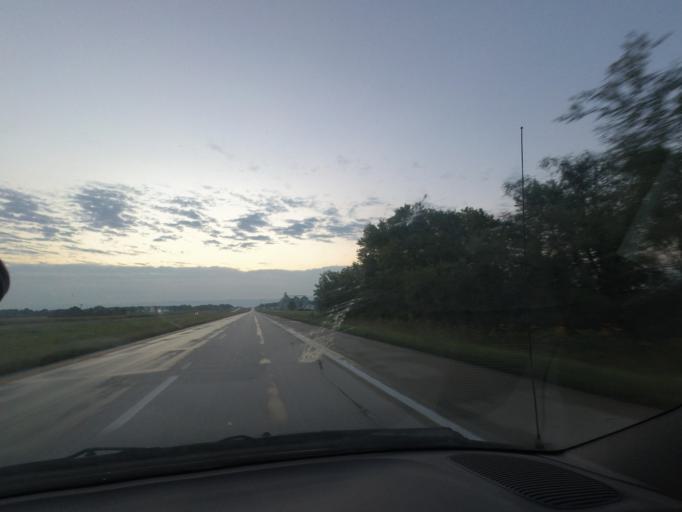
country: US
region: Missouri
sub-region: Macon County
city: Macon
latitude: 39.7598
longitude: -92.6813
